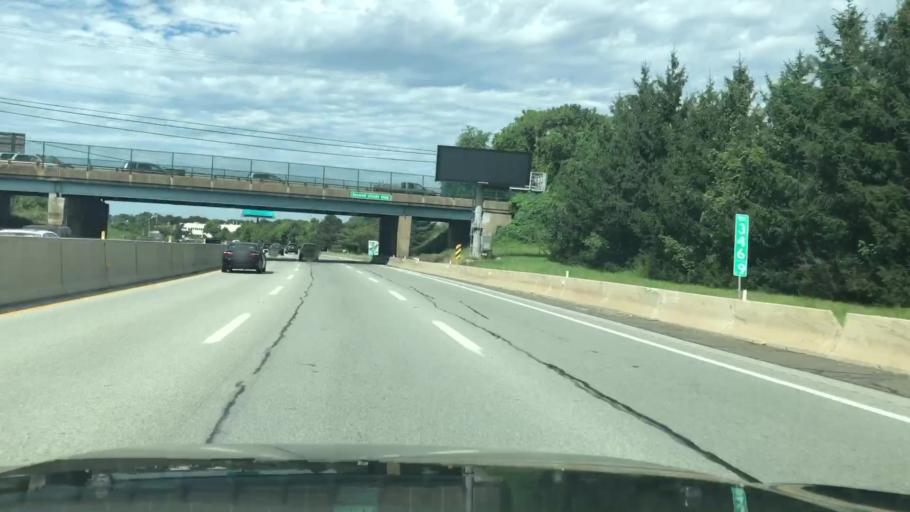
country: US
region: Pennsylvania
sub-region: Bucks County
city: Churchville
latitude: 40.1627
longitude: -75.0465
